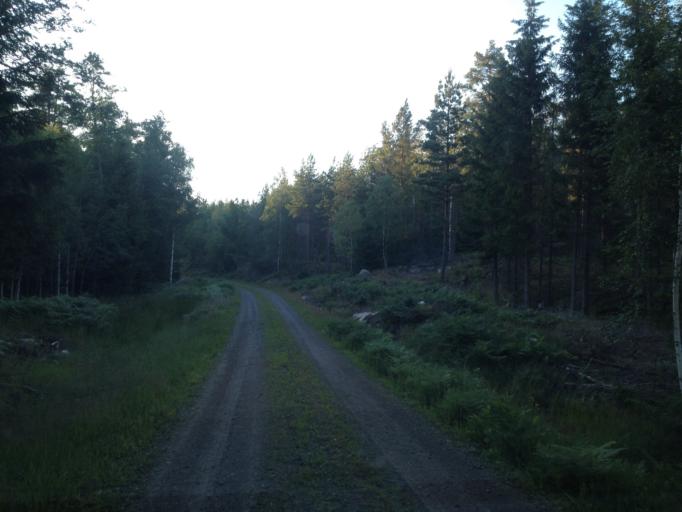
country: SE
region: Kalmar
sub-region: Vasterviks Kommun
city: Overum
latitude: 57.9963
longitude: 16.1687
